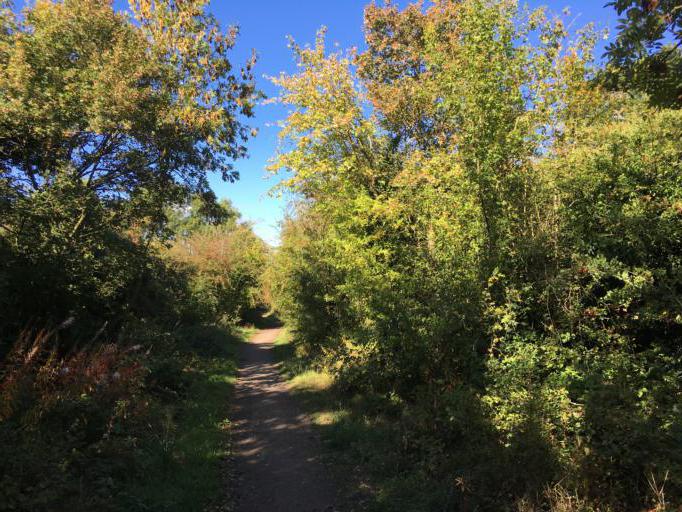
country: GB
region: England
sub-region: Solihull
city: Balsall Common
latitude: 52.3885
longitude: -1.6239
